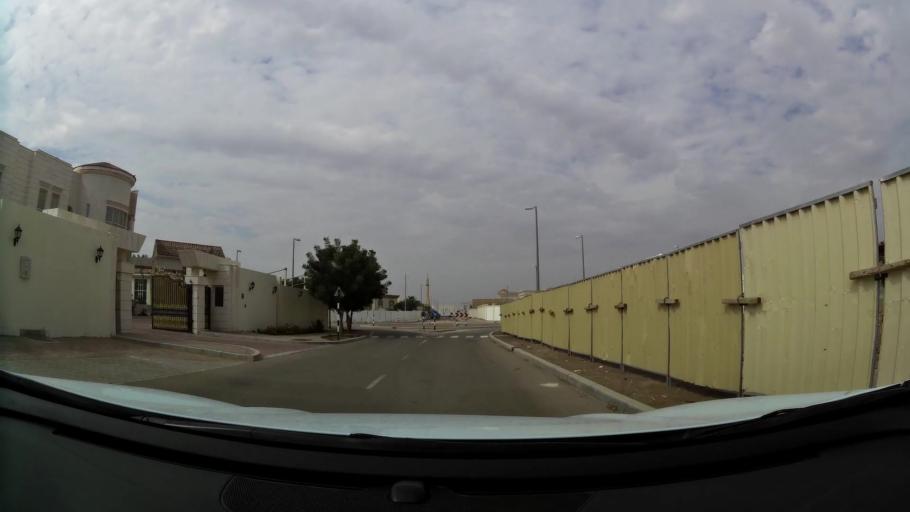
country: AE
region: Abu Dhabi
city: Al Ain
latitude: 24.1867
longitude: 55.8075
